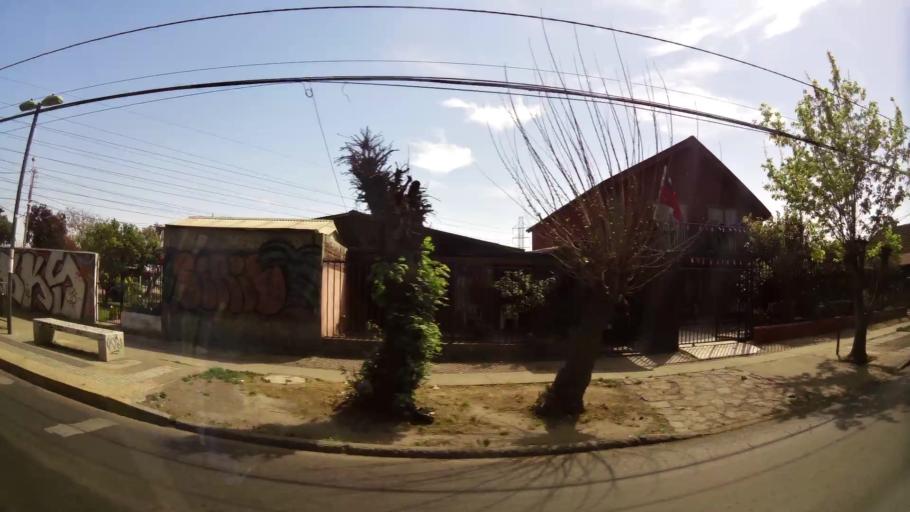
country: CL
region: Santiago Metropolitan
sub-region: Provincia de Santiago
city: Lo Prado
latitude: -33.4789
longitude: -70.7308
